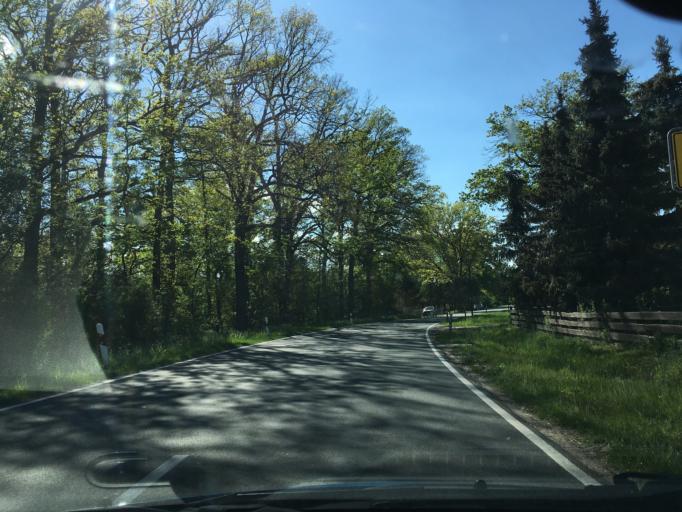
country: DE
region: Brandenburg
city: Lanz
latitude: 53.0154
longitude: 11.5475
